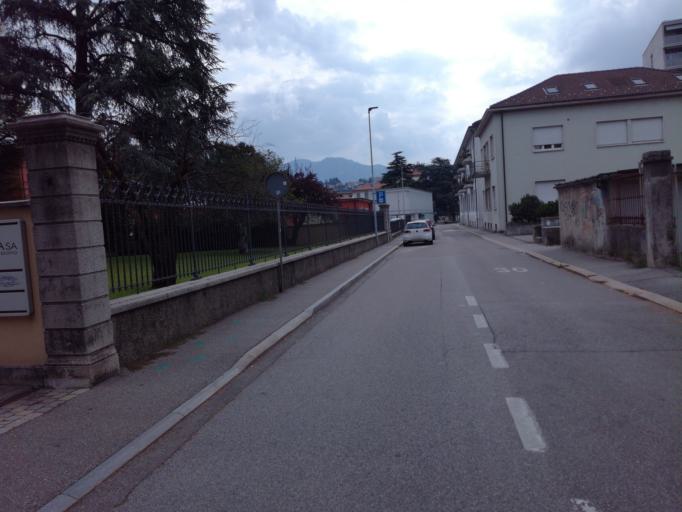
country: CH
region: Ticino
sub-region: Mendrisio District
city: Chiasso
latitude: 45.8373
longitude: 9.0249
